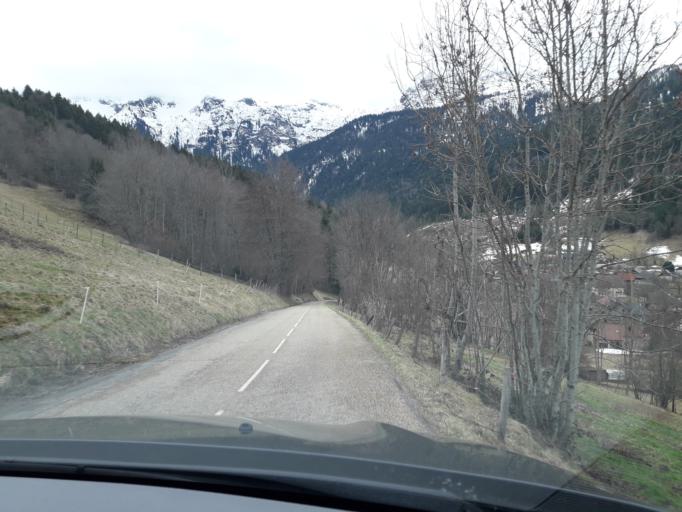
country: FR
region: Rhone-Alpes
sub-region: Departement de l'Isere
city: Le Champ-pres-Froges
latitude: 45.2426
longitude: 5.9744
